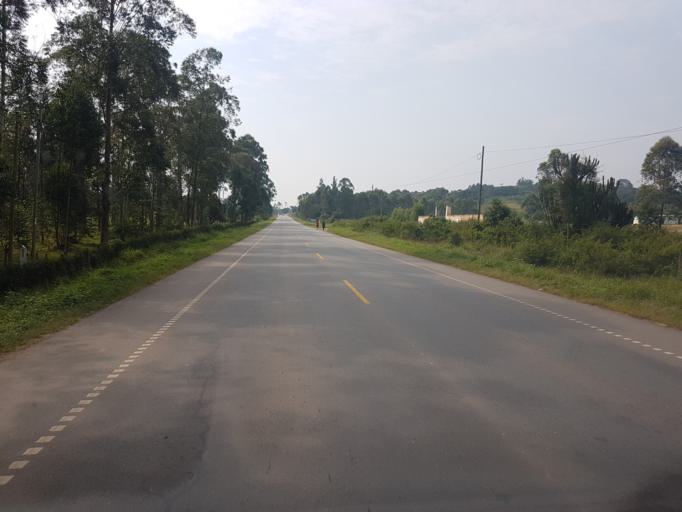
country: UG
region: Western Region
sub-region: Mbarara District
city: Bwizibwera
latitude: -0.6407
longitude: 30.5546
